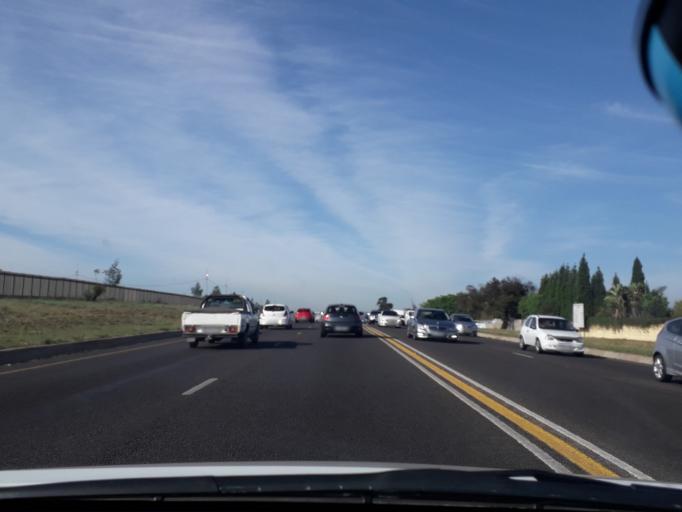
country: ZA
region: Gauteng
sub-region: City of Johannesburg Metropolitan Municipality
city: Roodepoort
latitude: -26.1070
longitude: 27.9231
